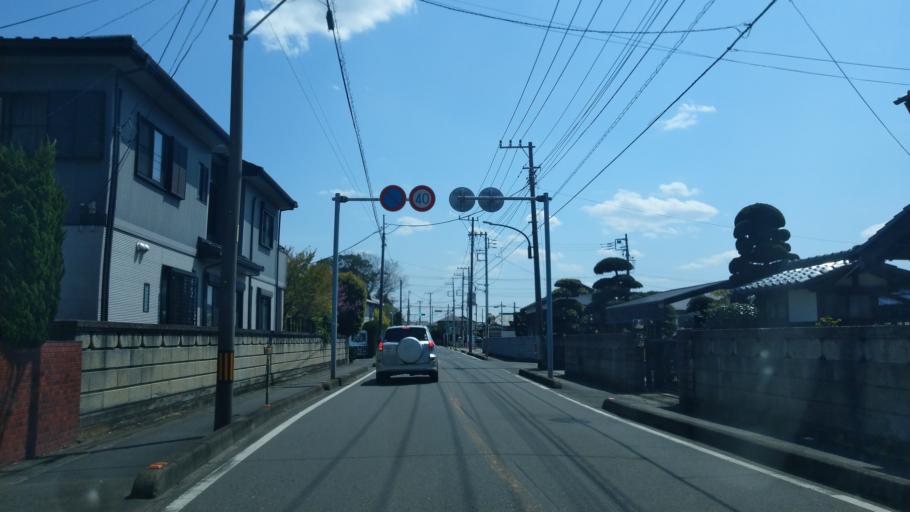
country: JP
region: Saitama
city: Yono
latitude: 35.8874
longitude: 139.6115
